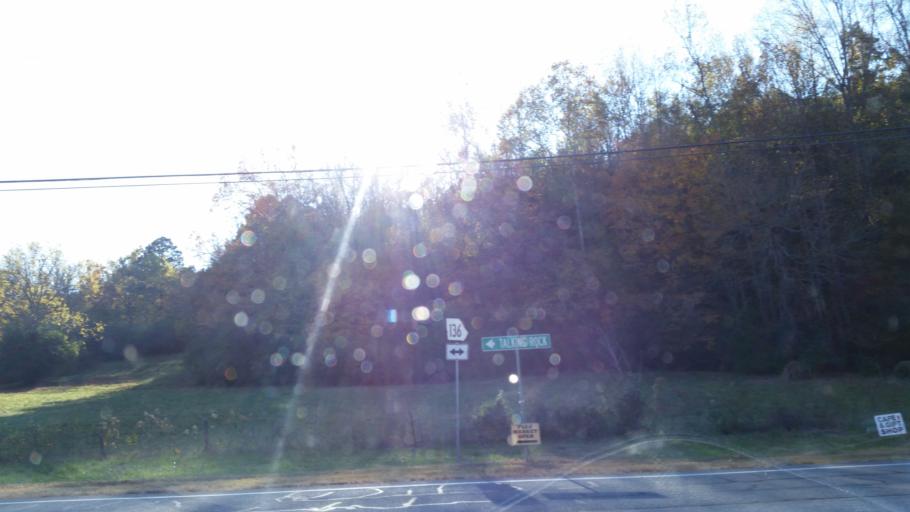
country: US
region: Georgia
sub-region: Pickens County
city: Jasper
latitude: 34.5179
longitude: -84.5220
